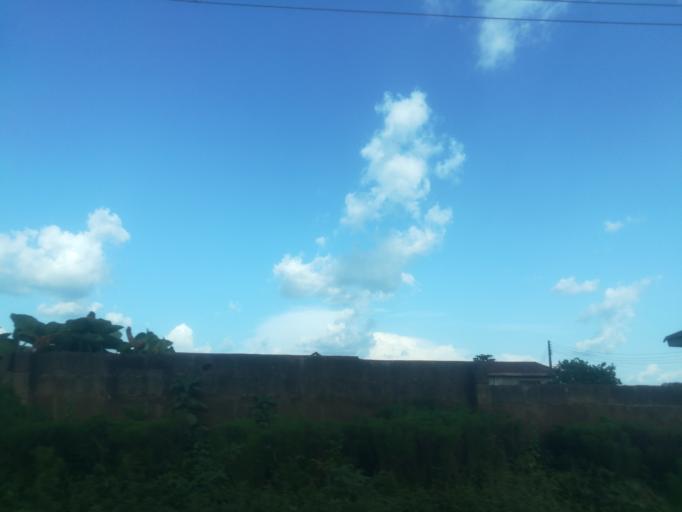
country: NG
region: Oyo
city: Lalupon
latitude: 7.4369
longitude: 3.9822
